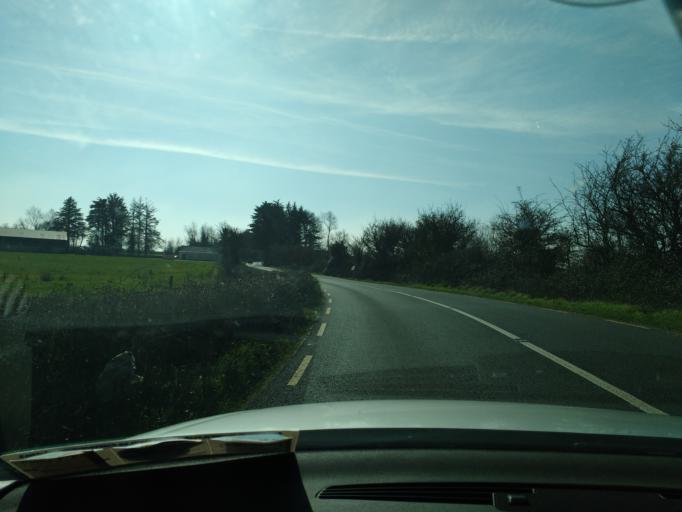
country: IE
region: Munster
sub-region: County Limerick
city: Castleconnell
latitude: 52.7003
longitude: -8.4600
